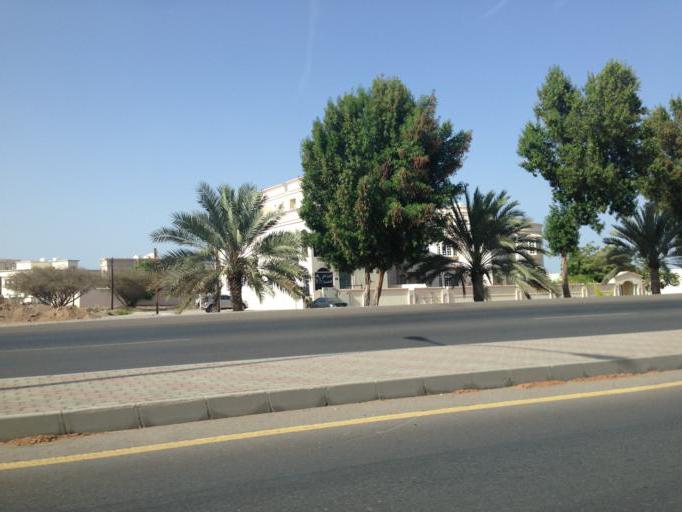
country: OM
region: Muhafazat Masqat
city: As Sib al Jadidah
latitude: 23.6129
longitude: 58.2354
